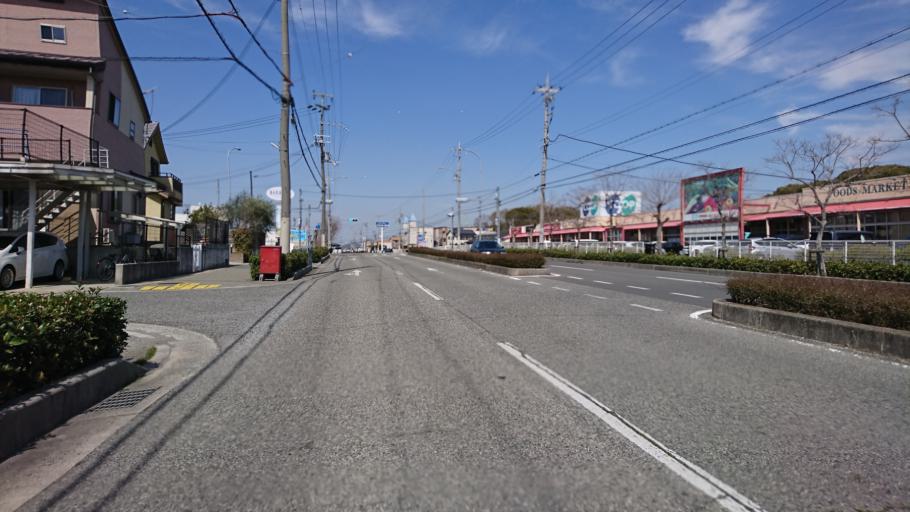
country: JP
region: Hyogo
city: Miki
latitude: 34.7471
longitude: 134.9152
